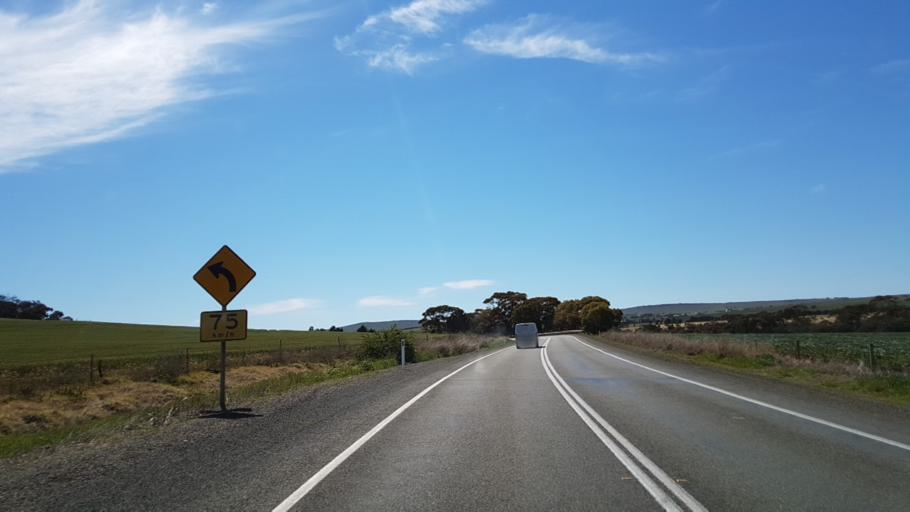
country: AU
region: South Australia
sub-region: Light
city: Freeling
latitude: -34.3431
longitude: 138.7822
